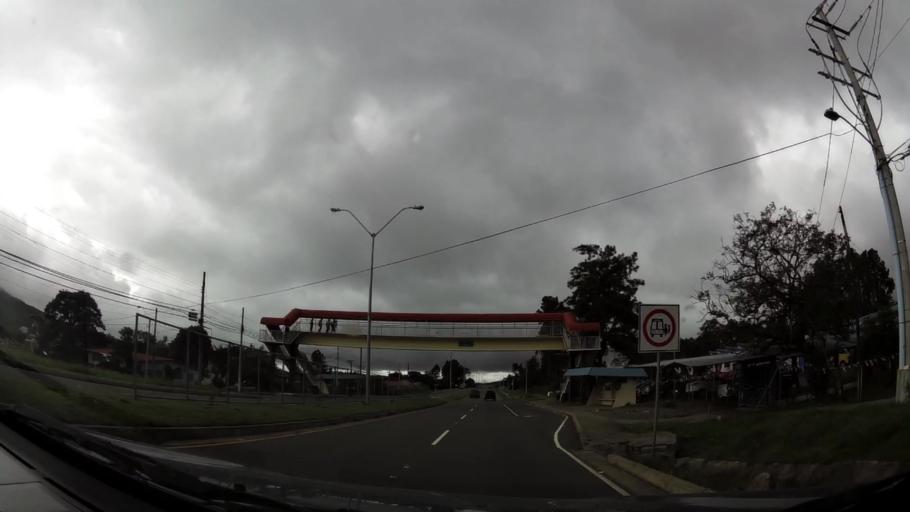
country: PA
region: Chiriqui
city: Palmira
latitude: 8.7456
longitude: -82.4326
